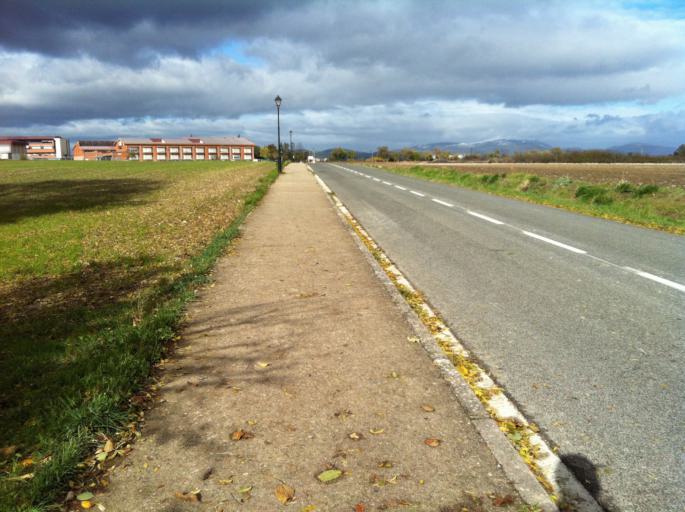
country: ES
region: Basque Country
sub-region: Provincia de Alava
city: Gasteiz / Vitoria
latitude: 42.8214
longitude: -2.6926
